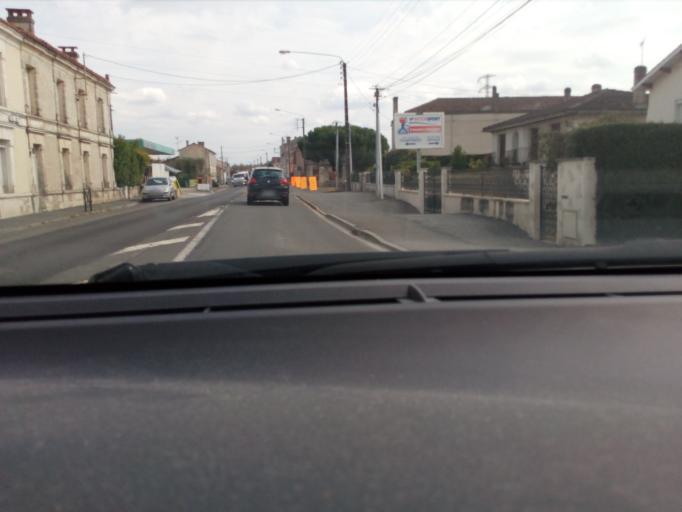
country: FR
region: Poitou-Charentes
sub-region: Departement de la Charente
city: Saint-Yrieix-sur-Charente
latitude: 45.6676
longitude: 0.1210
